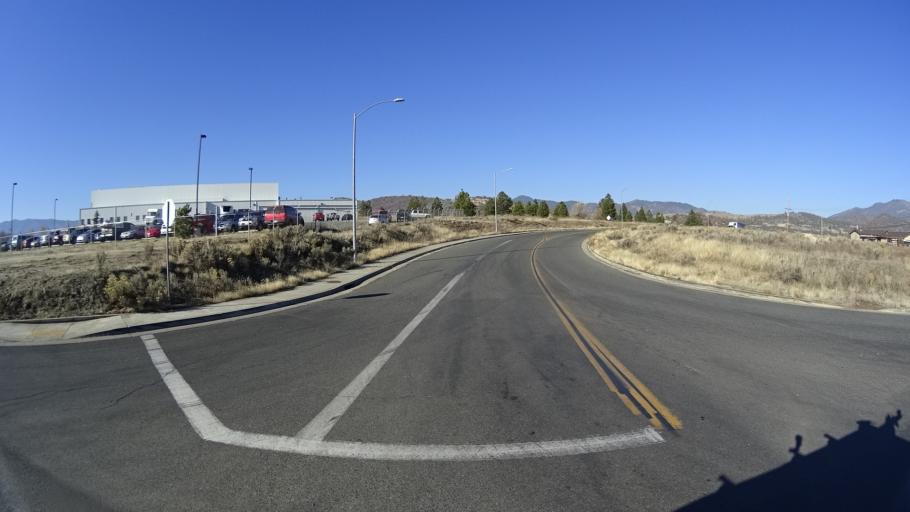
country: US
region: California
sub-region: Siskiyou County
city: Yreka
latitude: 41.7345
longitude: -122.5934
